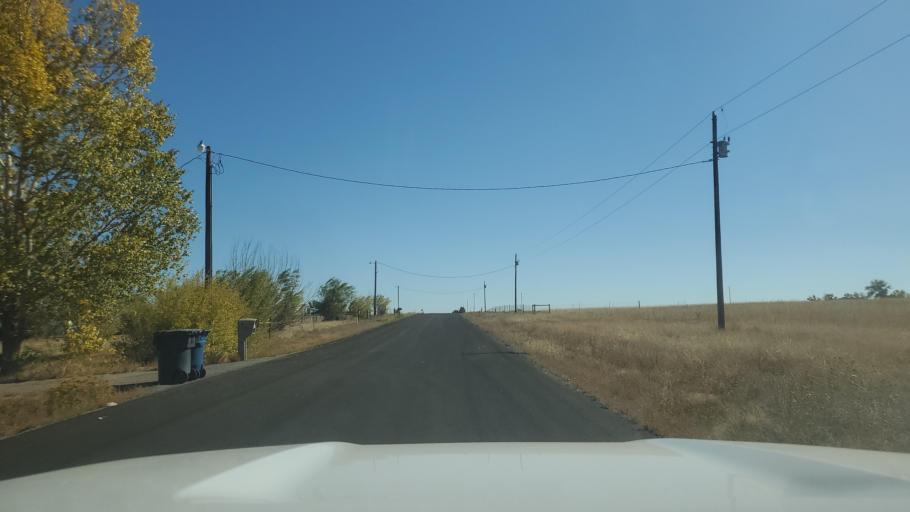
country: US
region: Colorado
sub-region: Adams County
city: Bennett
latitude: 39.7600
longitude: -104.3882
